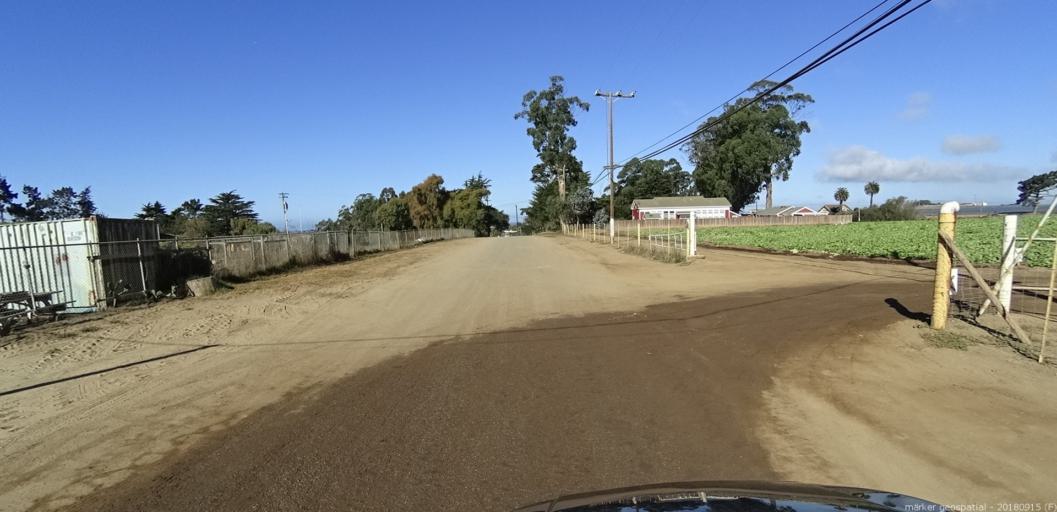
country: US
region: California
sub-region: Monterey County
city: Elkhorn
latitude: 36.8382
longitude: -121.7690
